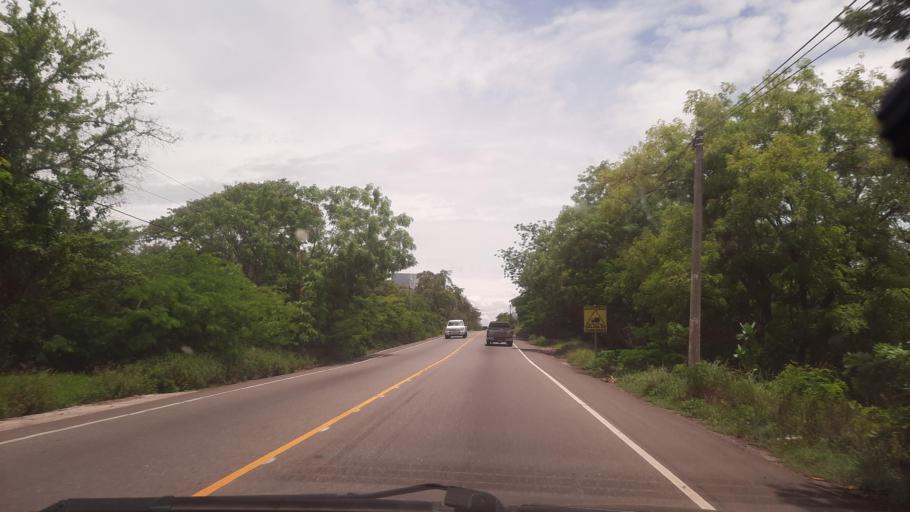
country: GT
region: Zacapa
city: Rio Hondo
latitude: 15.0464
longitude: -89.5714
